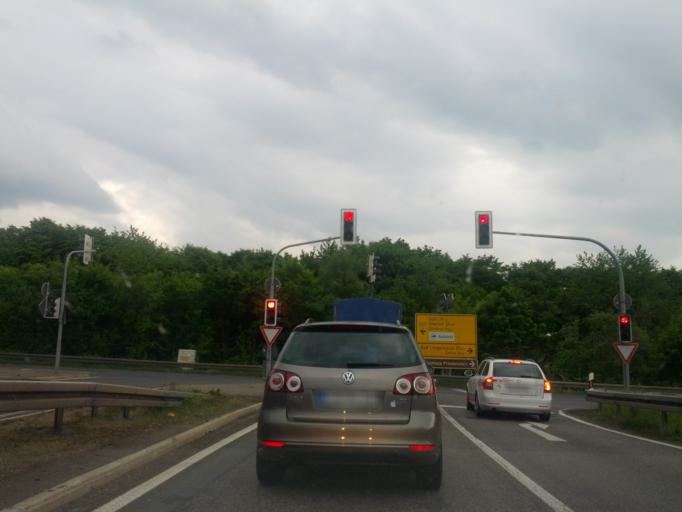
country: DE
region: Thuringia
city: Schwabhausen
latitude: 50.9033
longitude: 10.7288
